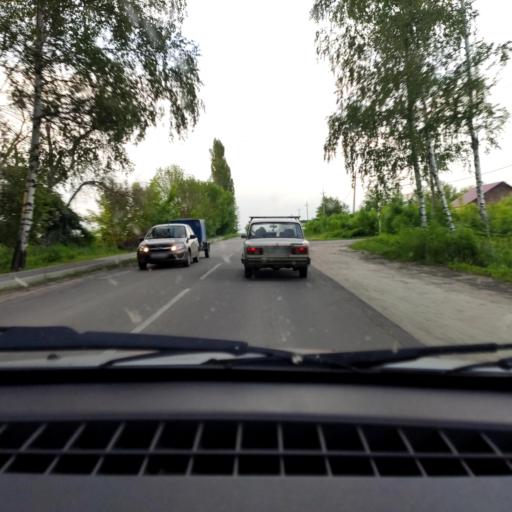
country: RU
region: Voronezj
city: Ramon'
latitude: 51.9416
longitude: 39.3514
